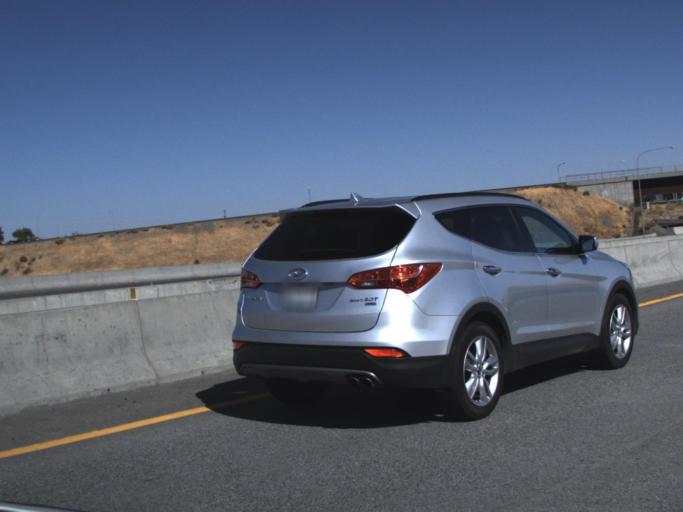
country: US
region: Washington
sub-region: Benton County
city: Richland
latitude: 46.2583
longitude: -119.2908
